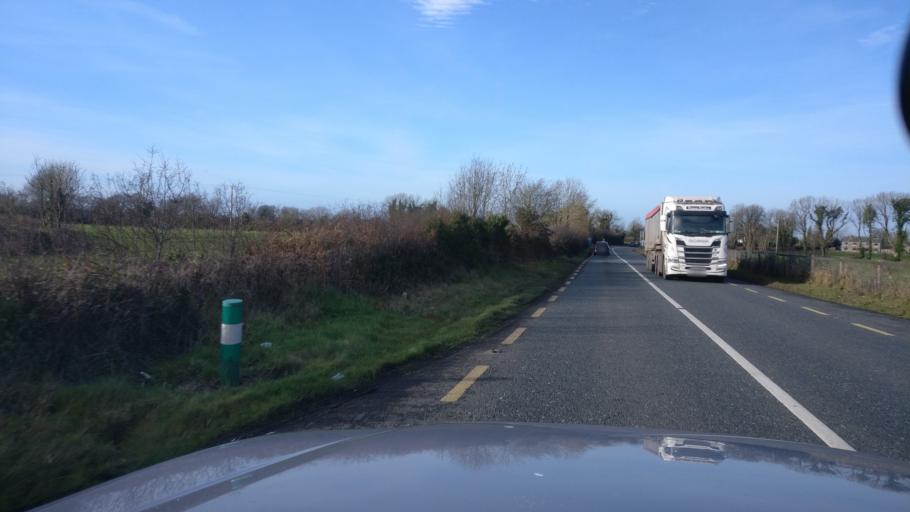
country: IE
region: Leinster
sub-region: Laois
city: Mountmellick
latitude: 53.1472
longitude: -7.3685
